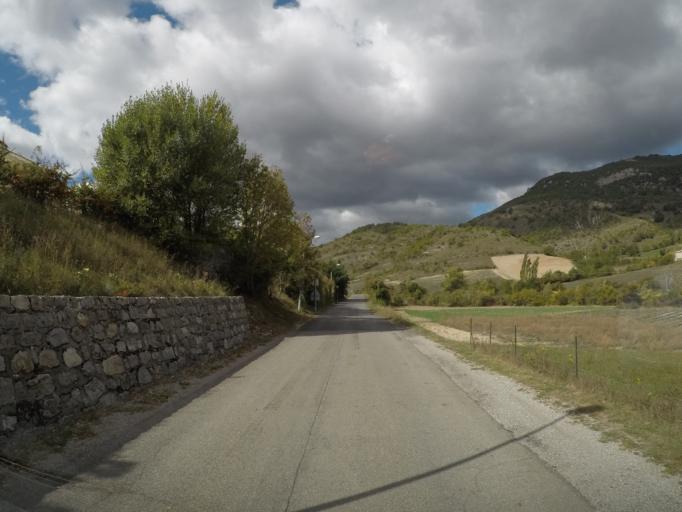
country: FR
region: Provence-Alpes-Cote d'Azur
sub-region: Departement du Vaucluse
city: Sault
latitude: 44.1721
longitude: 5.6075
